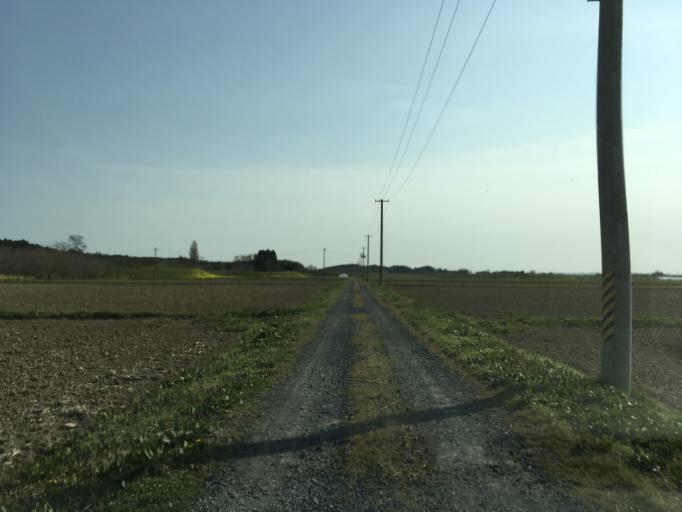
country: JP
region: Miyagi
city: Wakuya
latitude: 38.7134
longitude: 141.2779
